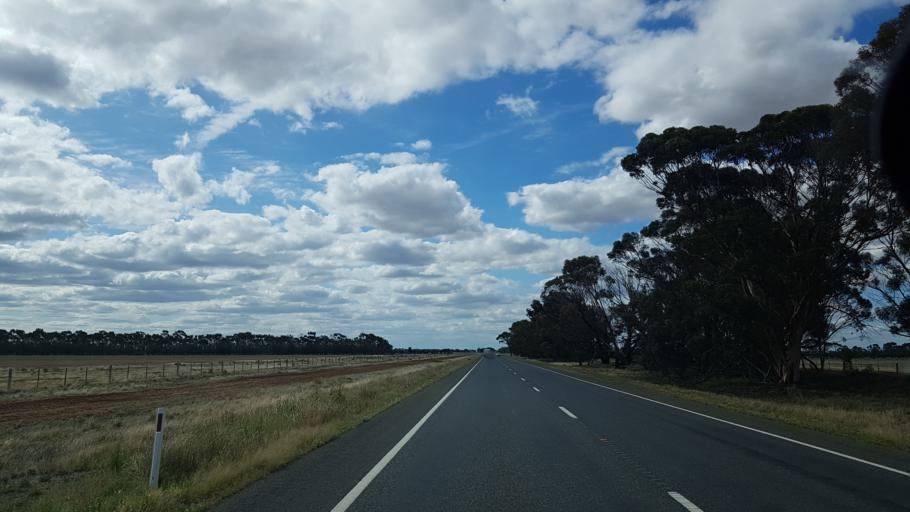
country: AU
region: Victoria
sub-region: Greater Bendigo
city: Long Gully
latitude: -36.0479
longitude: 143.9481
